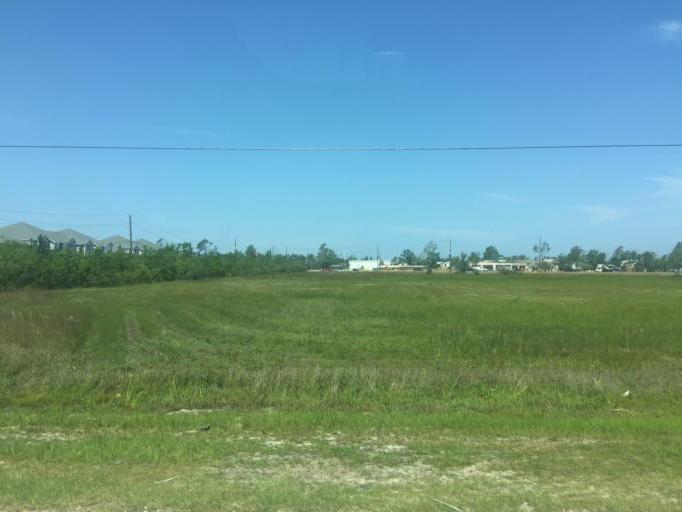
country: US
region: Florida
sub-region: Bay County
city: Lynn Haven
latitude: 30.2191
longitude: -85.6621
